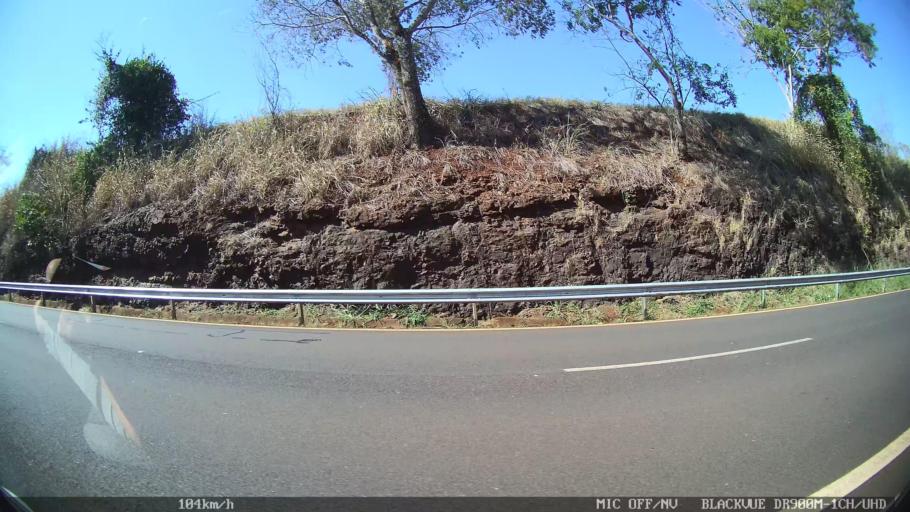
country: BR
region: Sao Paulo
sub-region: Franca
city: Franca
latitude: -20.6150
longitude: -47.4566
